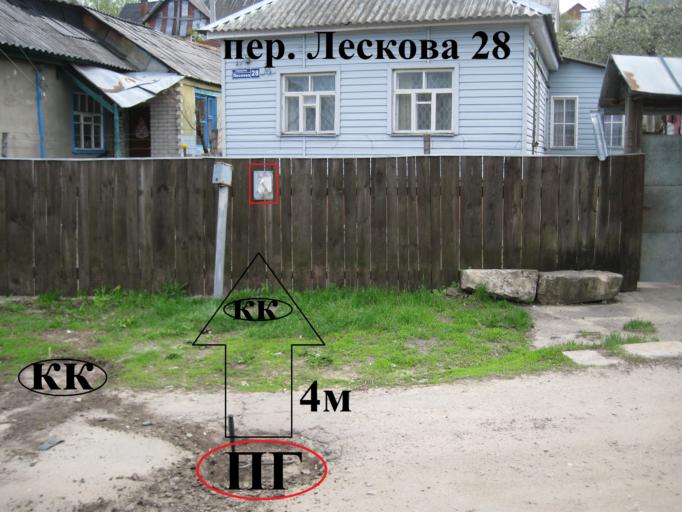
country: RU
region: Voronezj
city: Voronezh
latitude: 51.6384
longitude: 39.1954
